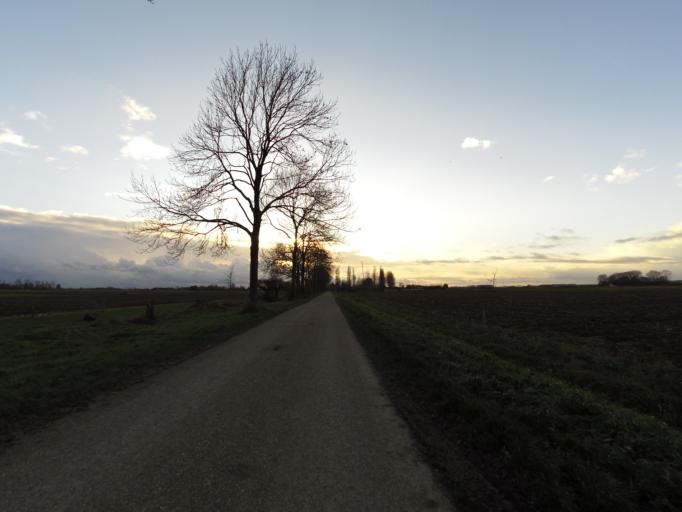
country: NL
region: Gelderland
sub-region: Oude IJsselstreek
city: Gendringen
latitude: 51.8715
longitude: 6.3471
